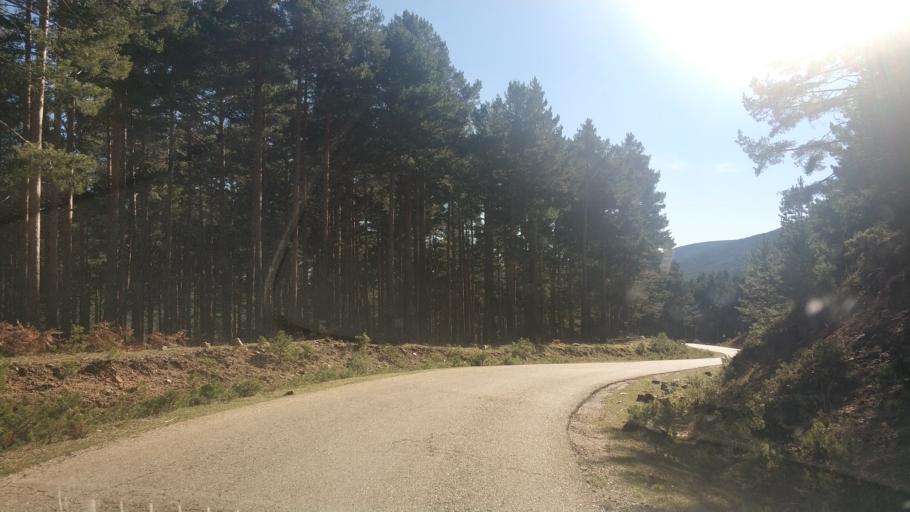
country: ES
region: La Rioja
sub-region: Provincia de La Rioja
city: Viniegra de Arriba
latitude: 42.0005
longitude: -2.8051
